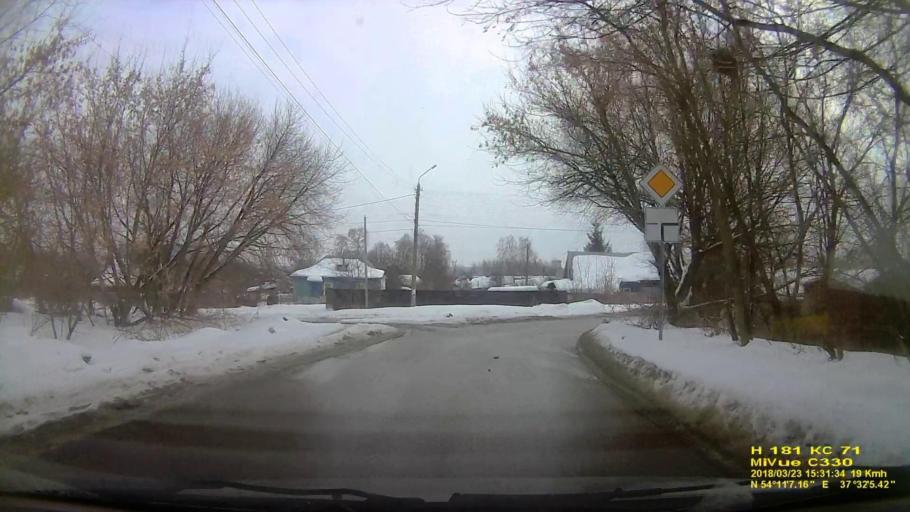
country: RU
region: Tula
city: Kosaya Gora
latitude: 54.1854
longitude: 37.5348
